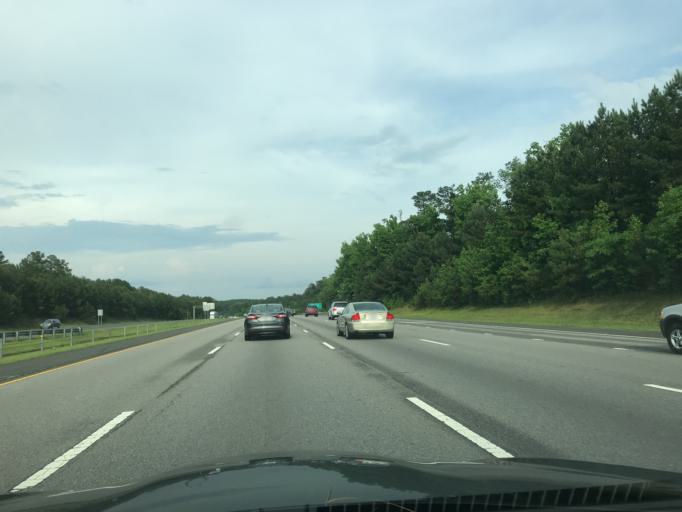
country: US
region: North Carolina
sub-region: Wake County
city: Morrisville
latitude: 35.8945
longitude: -78.8020
